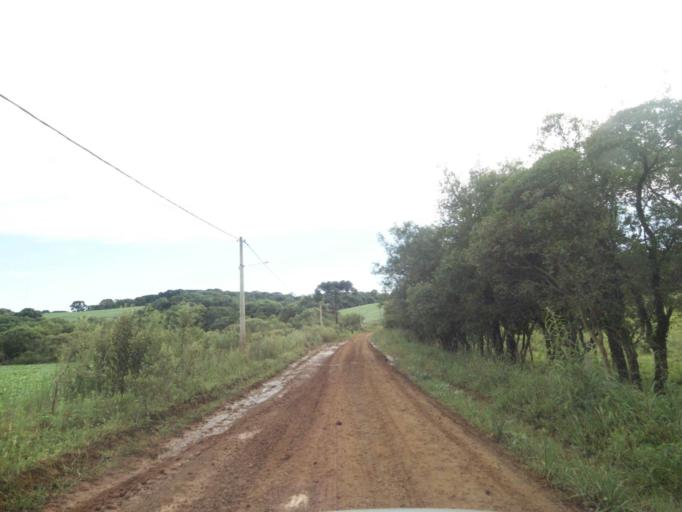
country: BR
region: Rio Grande do Sul
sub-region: Lagoa Vermelha
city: Lagoa Vermelha
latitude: -28.2403
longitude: -51.5048
